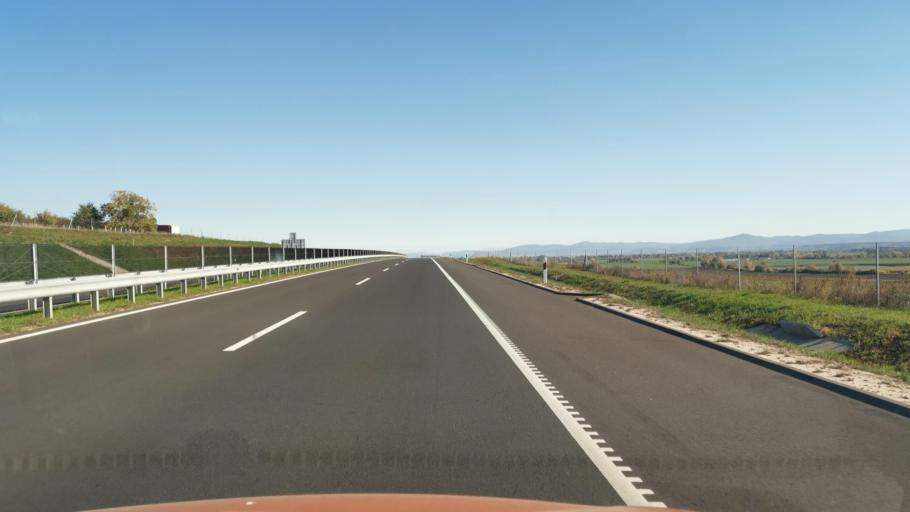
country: HU
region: Borsod-Abauj-Zemplen
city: Halmaj
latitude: 48.2592
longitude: 20.9854
